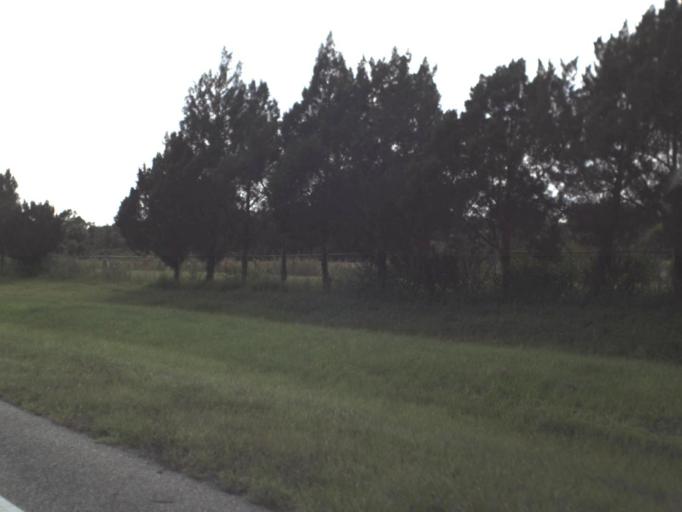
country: US
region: Florida
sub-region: Lee County
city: Alva
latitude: 26.7093
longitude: -81.6295
